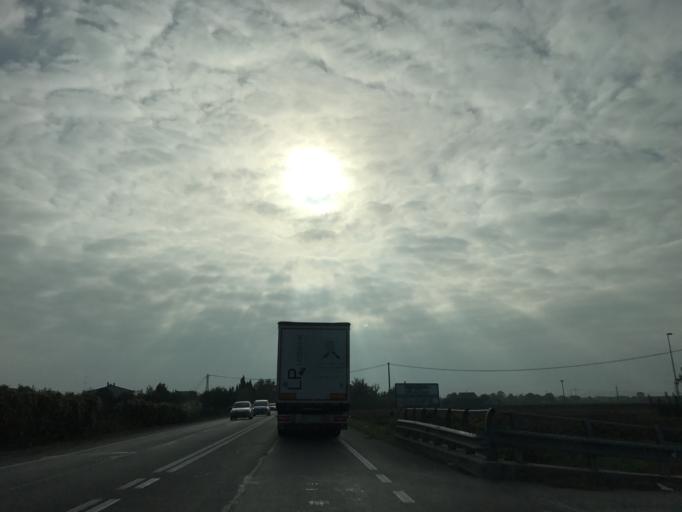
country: IT
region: Emilia-Romagna
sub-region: Provincia di Rimini
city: Santa Giustina
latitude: 44.0947
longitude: 12.5049
